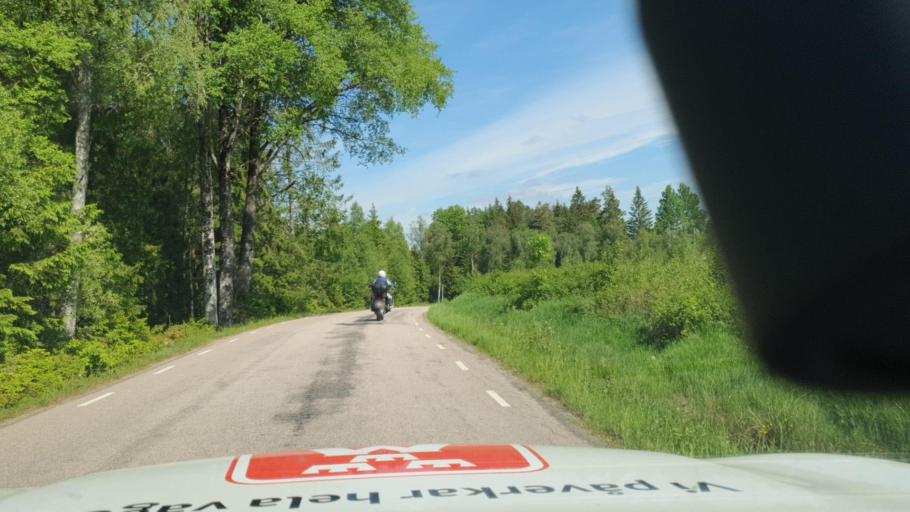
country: SE
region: Vaestra Goetaland
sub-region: Herrljunga Kommun
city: Herrljunga
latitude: 58.0163
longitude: 13.0944
